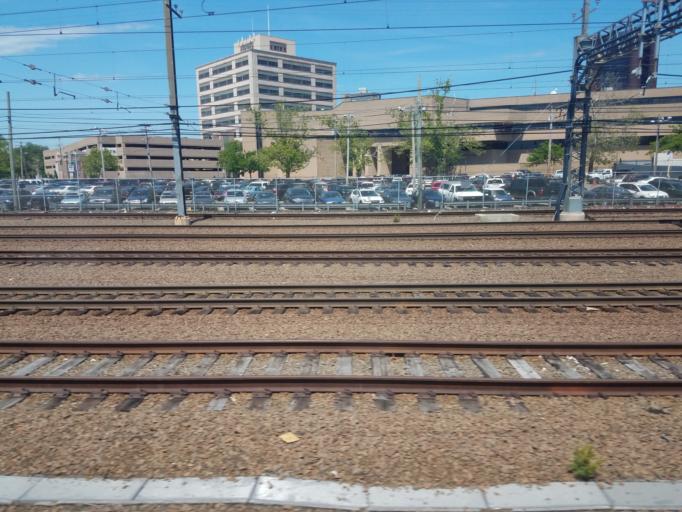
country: US
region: Connecticut
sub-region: New Haven County
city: New Haven
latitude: 41.2993
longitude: -72.9242
